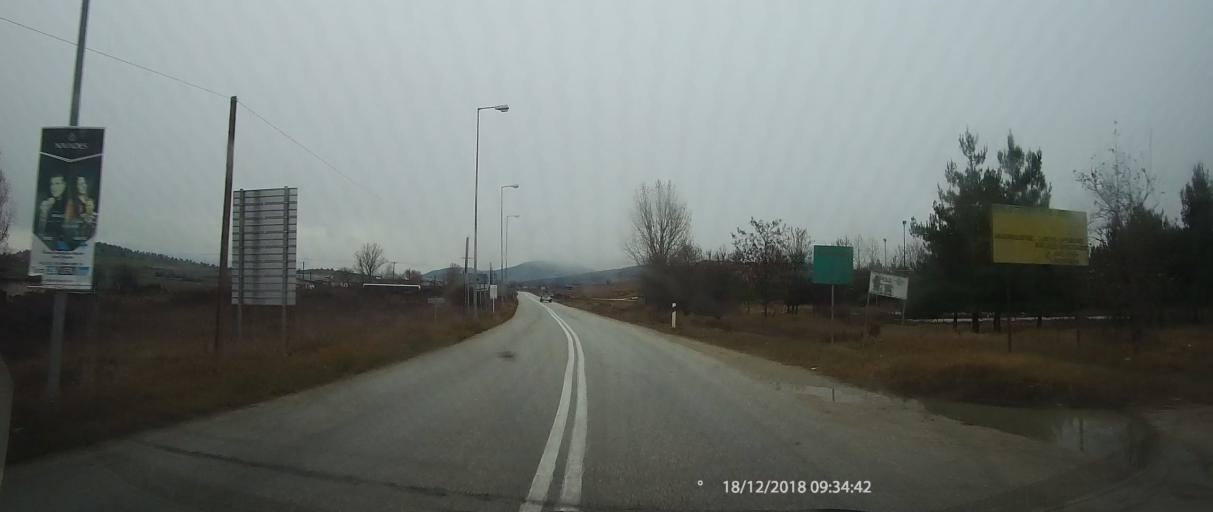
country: GR
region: Thessaly
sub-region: Nomos Larisis
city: Elassona
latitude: 39.9763
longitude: 22.1841
